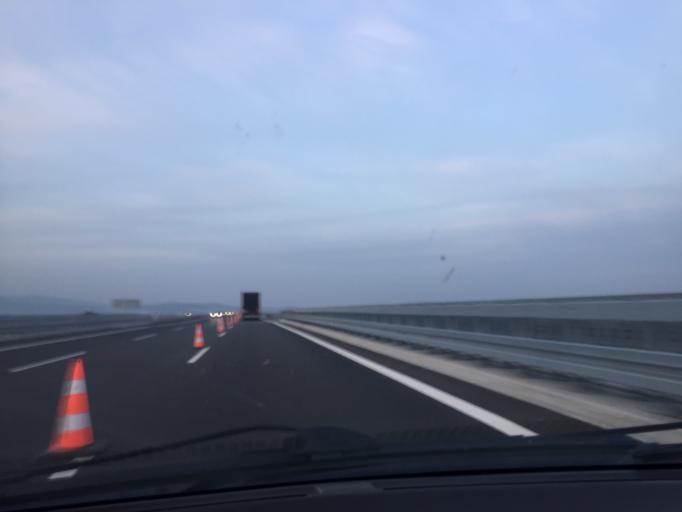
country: TR
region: Manisa
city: Halitpasa
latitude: 38.7351
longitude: 27.6568
